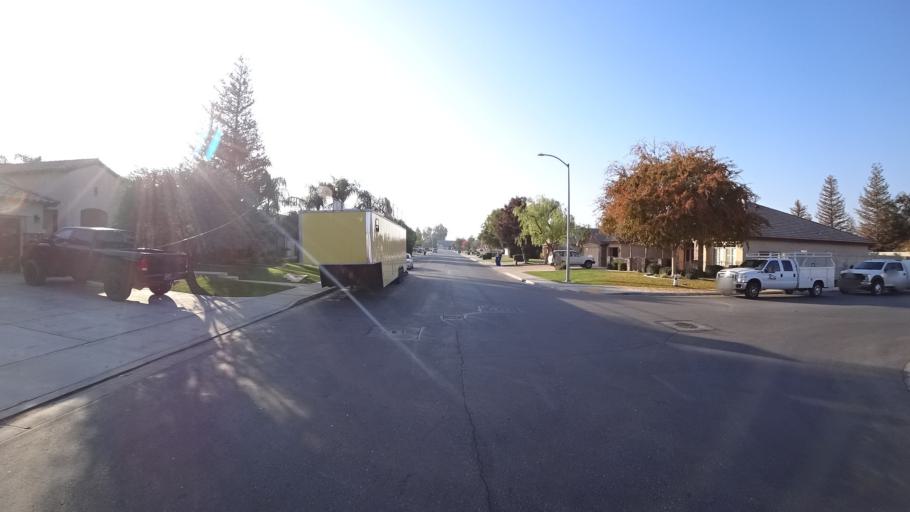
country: US
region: California
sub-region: Kern County
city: Rosedale
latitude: 35.3816
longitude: -119.1490
